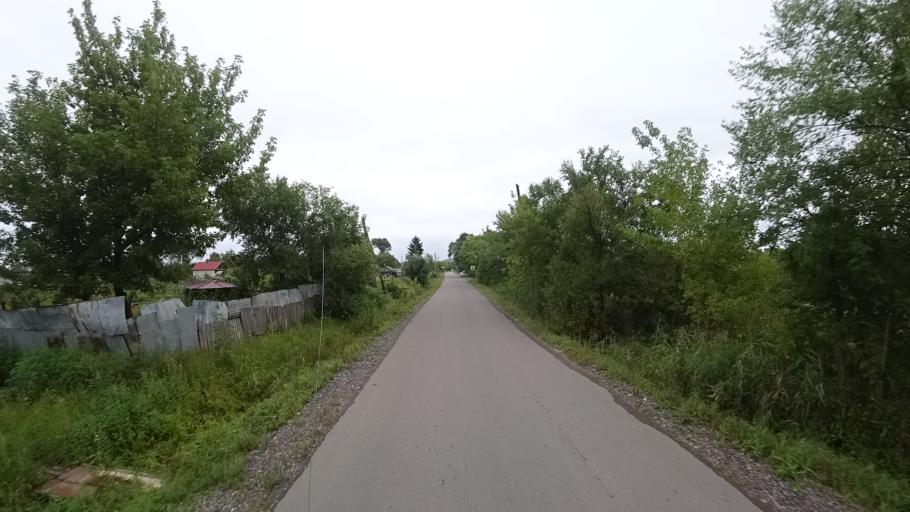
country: RU
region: Primorskiy
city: Chernigovka
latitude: 44.3397
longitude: 132.5363
